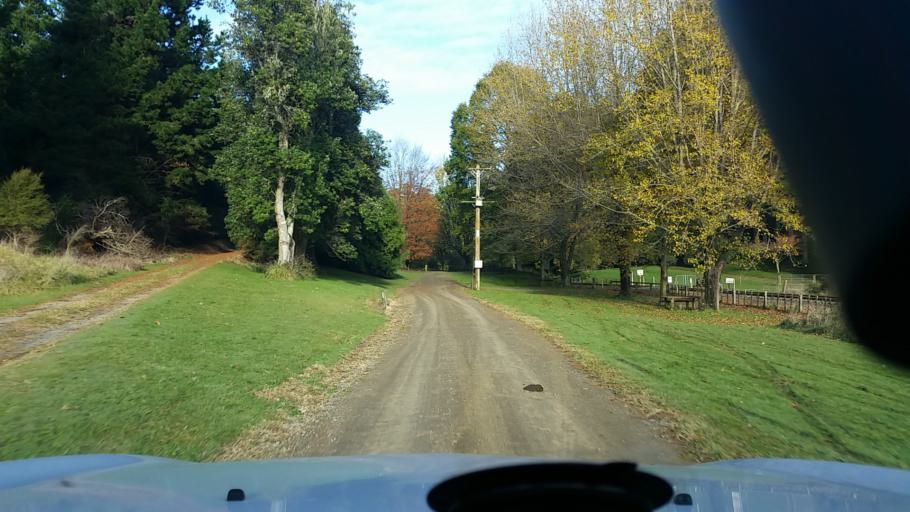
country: NZ
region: Hawke's Bay
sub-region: Napier City
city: Napier
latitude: -39.2421
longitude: 176.8091
